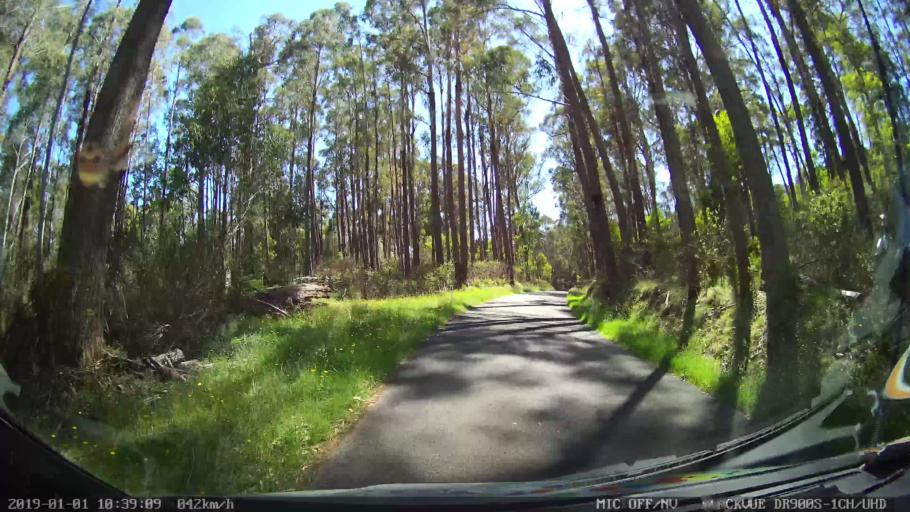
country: AU
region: New South Wales
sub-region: Snowy River
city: Jindabyne
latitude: -36.0413
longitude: 148.3021
